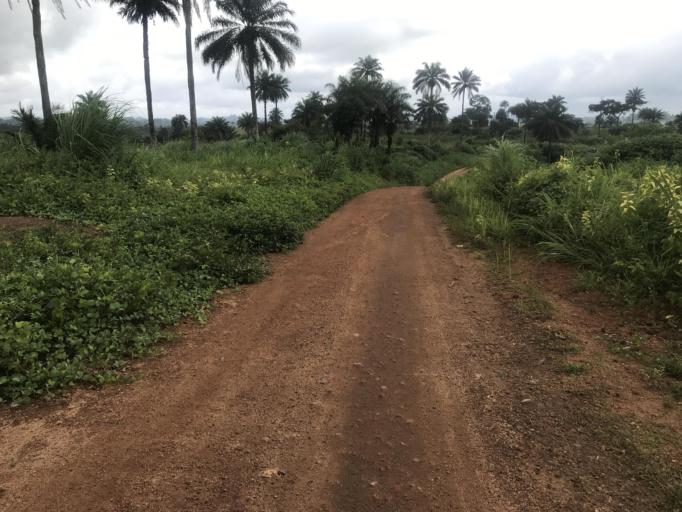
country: GN
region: Nzerekore
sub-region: Prefecture de Guekedou
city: Gueckedou
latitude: 8.4772
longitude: -10.2969
